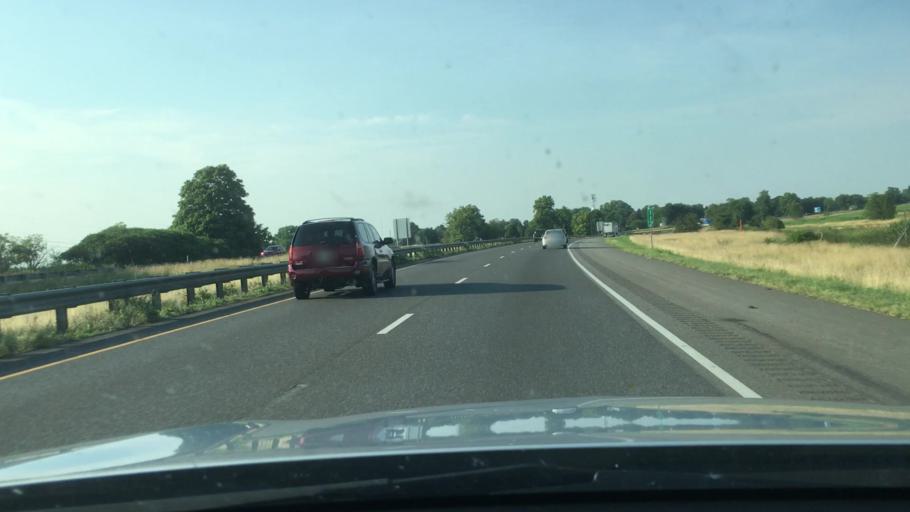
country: US
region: Maryland
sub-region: Washington County
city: Maugansville
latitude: 39.7108
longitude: -77.7424
